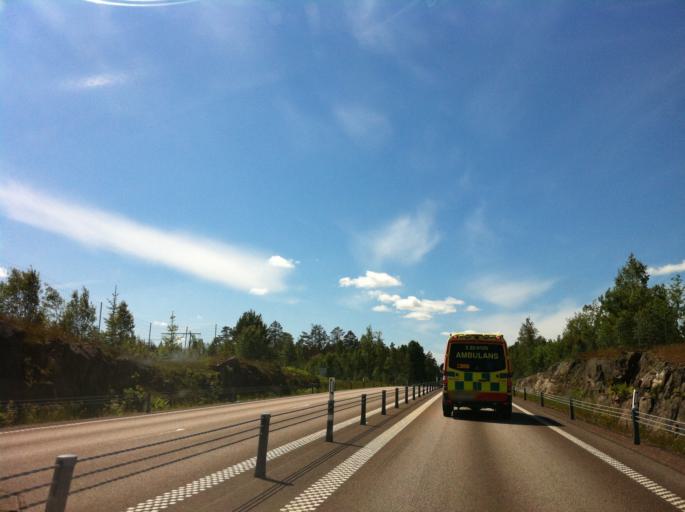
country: SE
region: Vaestra Goetaland
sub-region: Melleruds Kommun
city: Mellerud
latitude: 58.8456
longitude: 12.5502
